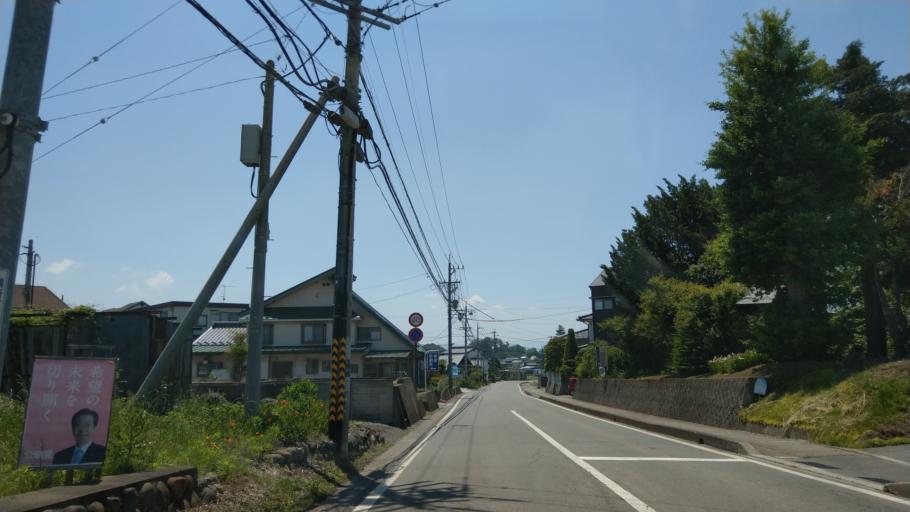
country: JP
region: Nagano
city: Komoro
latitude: 36.2908
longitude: 138.4403
